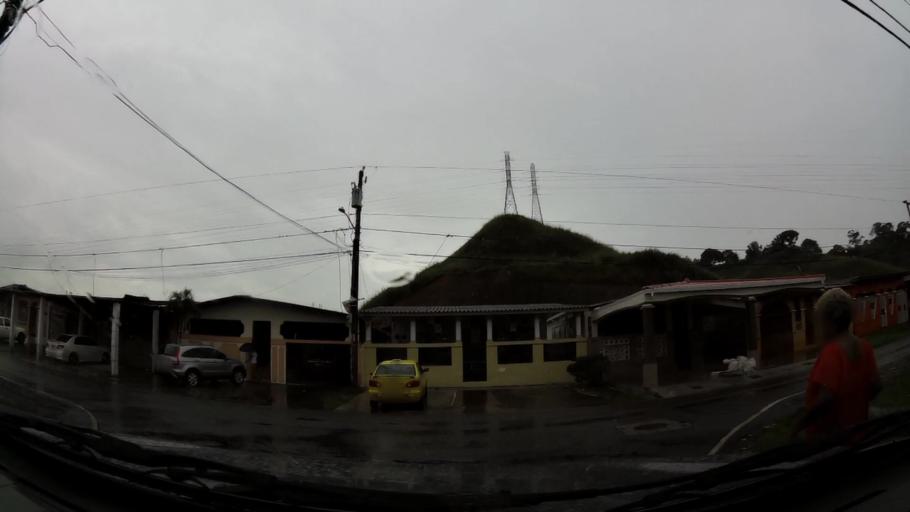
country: PA
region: Colon
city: Sabanitas
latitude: 9.3536
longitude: -79.8086
